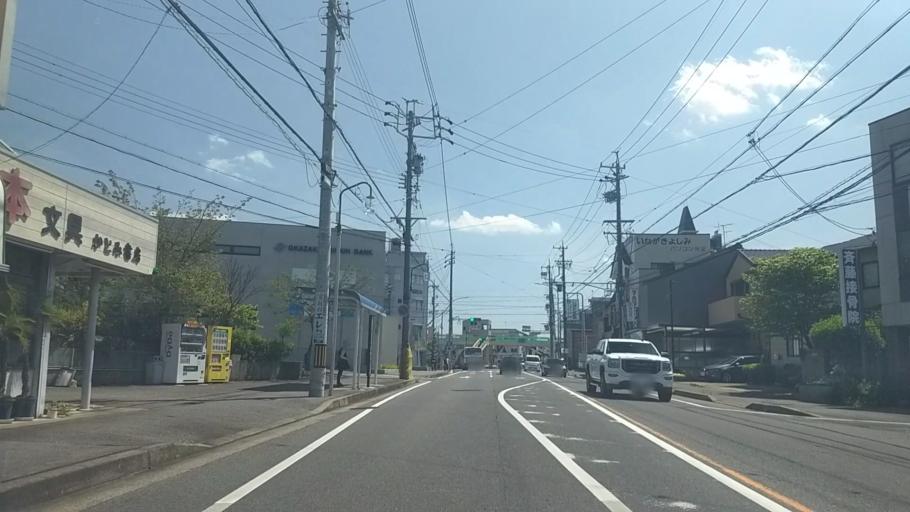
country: JP
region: Aichi
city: Okazaki
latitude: 34.9779
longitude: 137.1694
